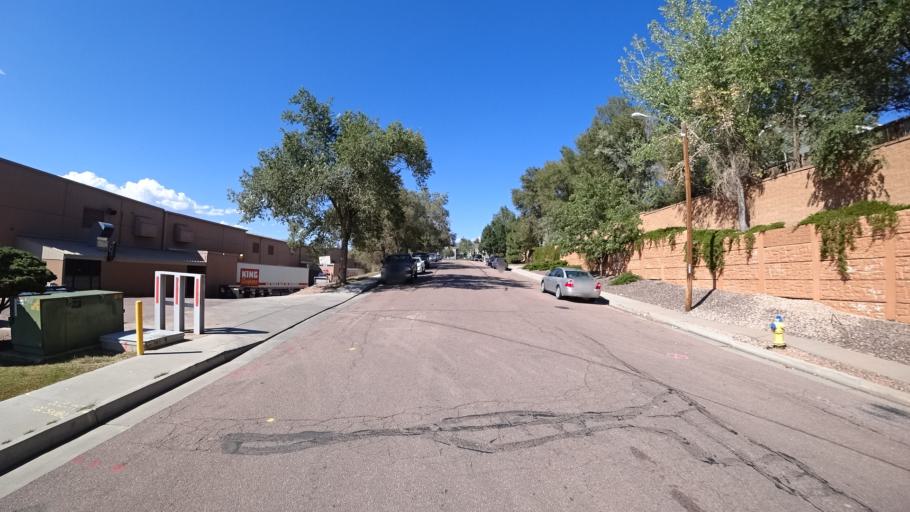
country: US
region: Colorado
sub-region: El Paso County
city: Colorado Springs
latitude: 38.8485
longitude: -104.8465
